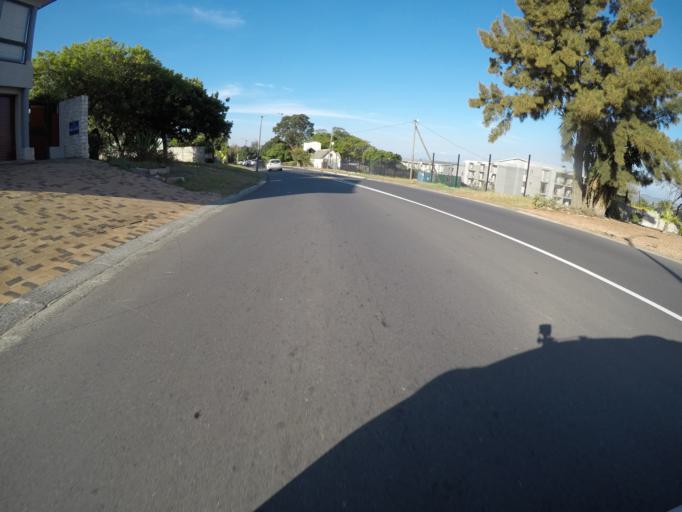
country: ZA
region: Western Cape
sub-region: City of Cape Town
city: Kraaifontein
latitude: -33.8733
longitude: 18.6479
